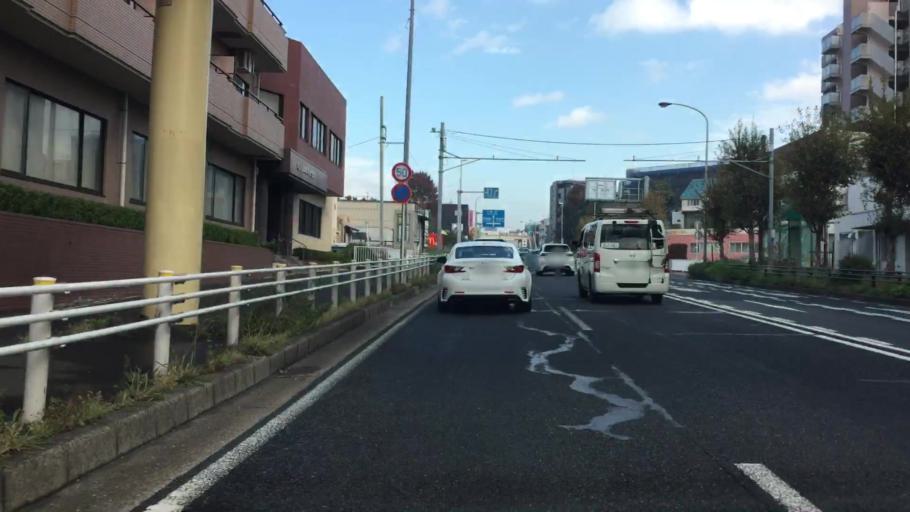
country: JP
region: Chiba
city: Matsudo
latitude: 35.8120
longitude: 139.9226
